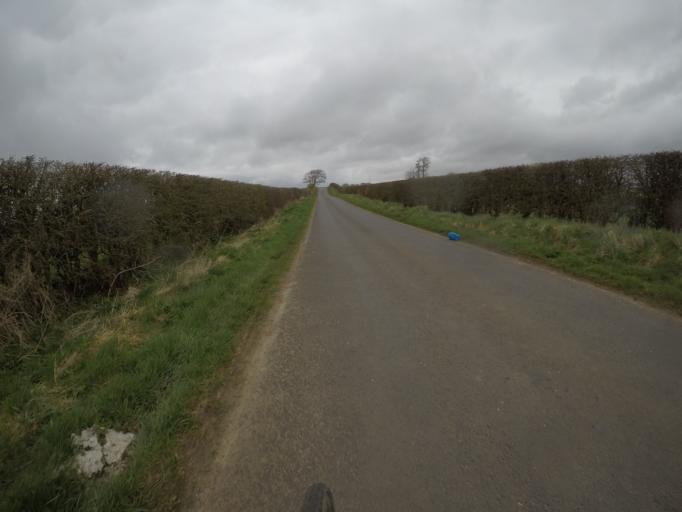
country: GB
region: Scotland
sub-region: East Ayrshire
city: Galston
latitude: 55.6183
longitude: -4.4349
